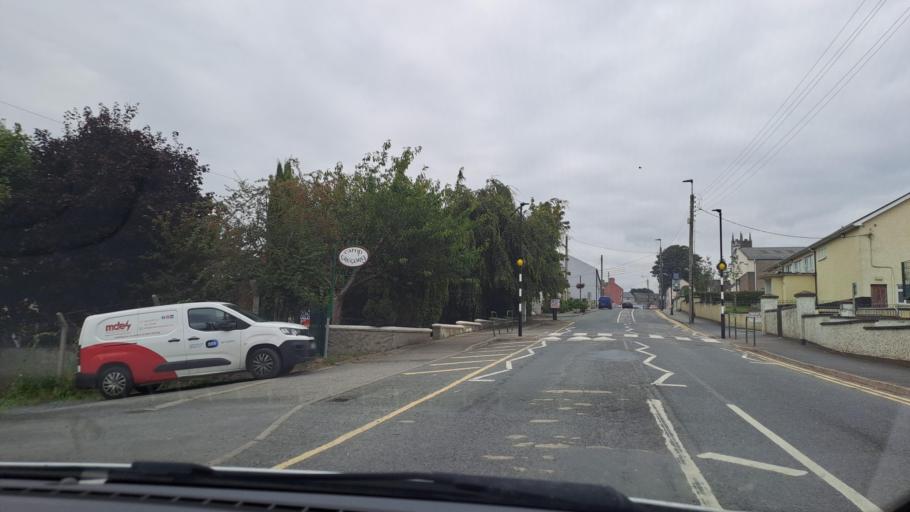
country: IE
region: Ulster
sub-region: An Cabhan
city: Bailieborough
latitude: 53.9924
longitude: -6.8936
